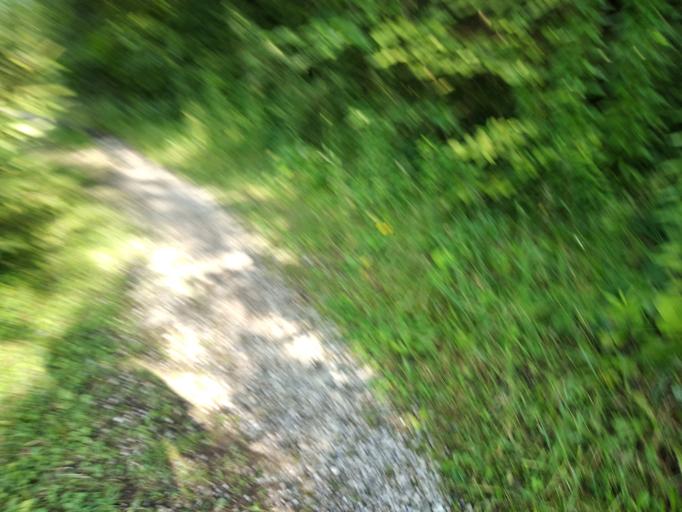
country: DE
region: Bavaria
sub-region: Upper Bavaria
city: Neubiberg
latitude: 48.0930
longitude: 11.6682
